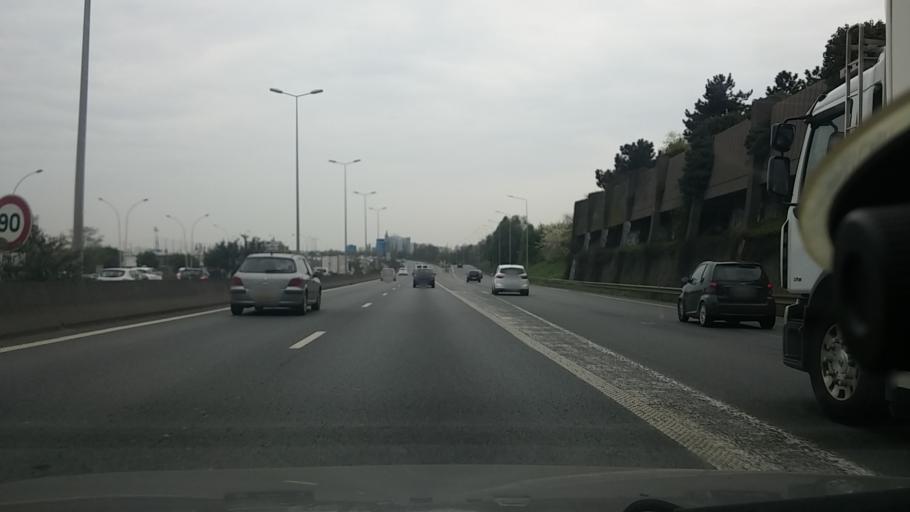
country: FR
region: Ile-de-France
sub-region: Departement du Val-de-Marne
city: L'Hay-les-Roses
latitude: 48.7791
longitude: 2.3468
